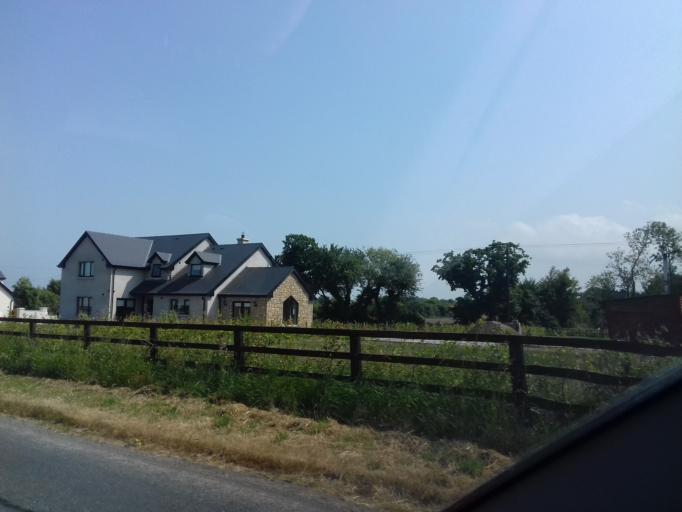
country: IE
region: Leinster
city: Balrothery
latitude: 53.5972
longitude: -6.2299
